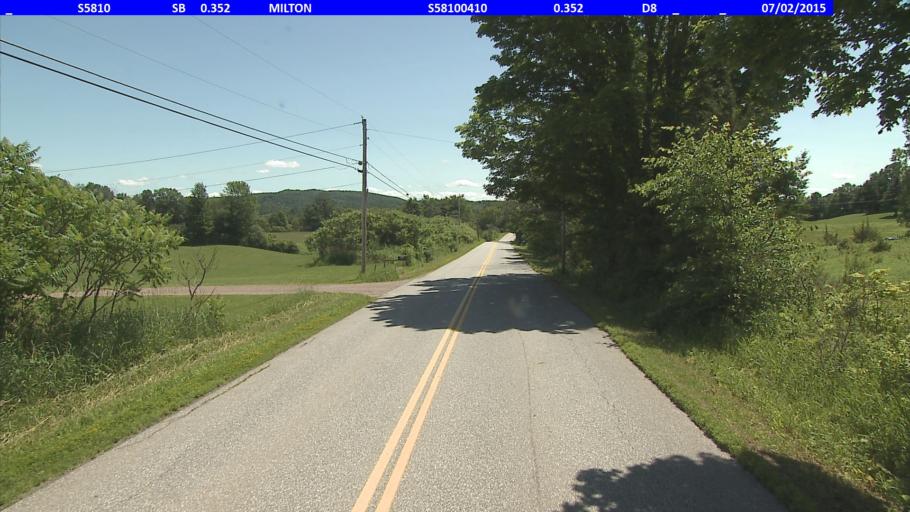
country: US
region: Vermont
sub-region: Chittenden County
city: Colchester
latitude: 44.5869
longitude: -73.1301
